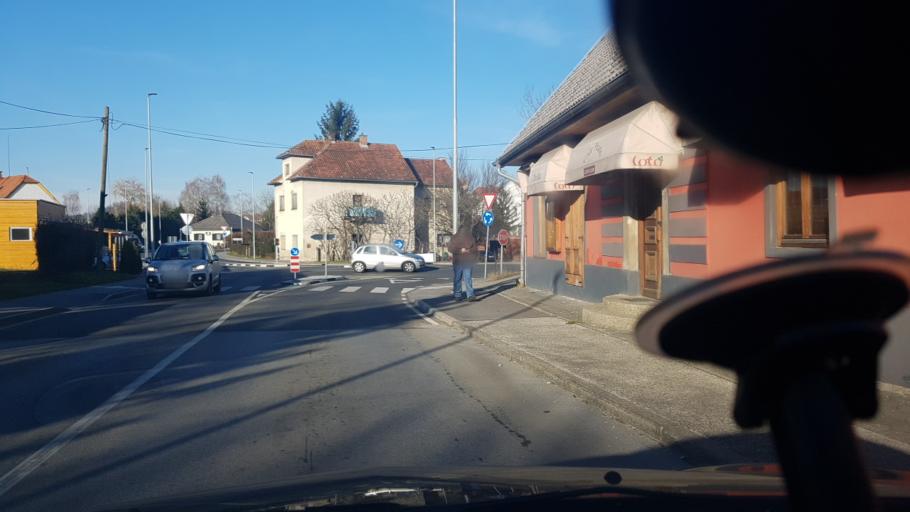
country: SI
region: Ptuj
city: Ptuj
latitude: 46.4146
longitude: 15.8645
